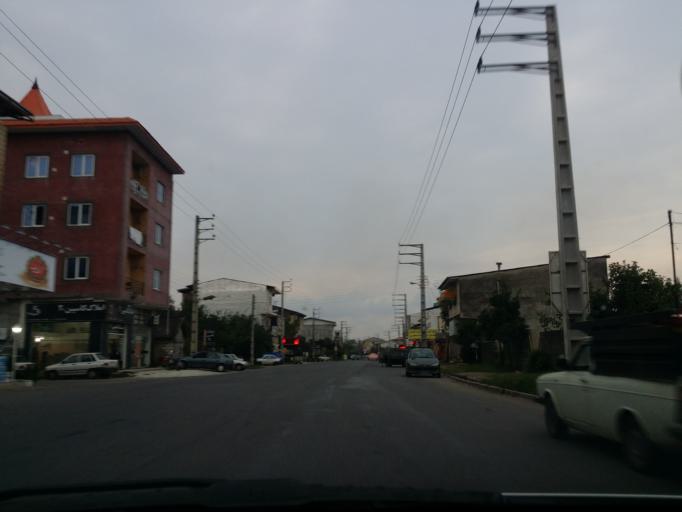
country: IR
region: Mazandaran
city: `Abbasabad
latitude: 36.7110
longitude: 51.1007
